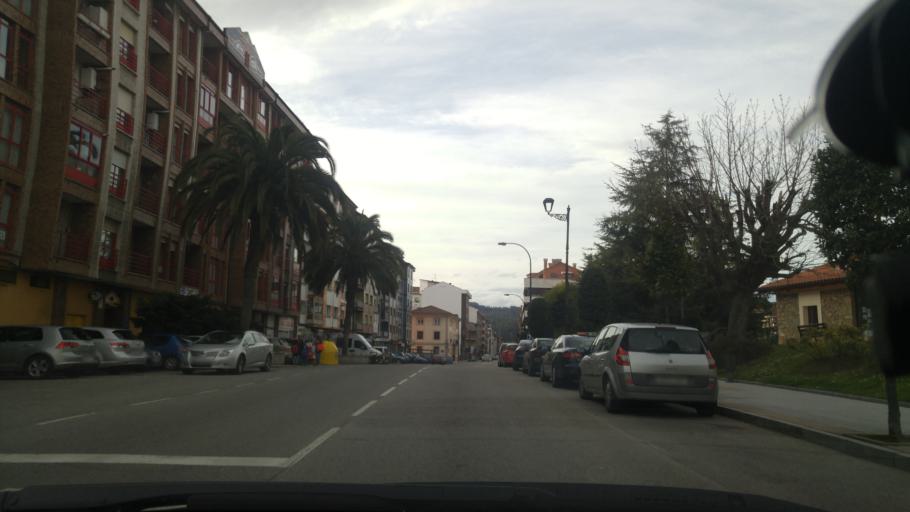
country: ES
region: Asturias
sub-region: Province of Asturias
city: Llanera
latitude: 43.4386
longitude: -5.8500
